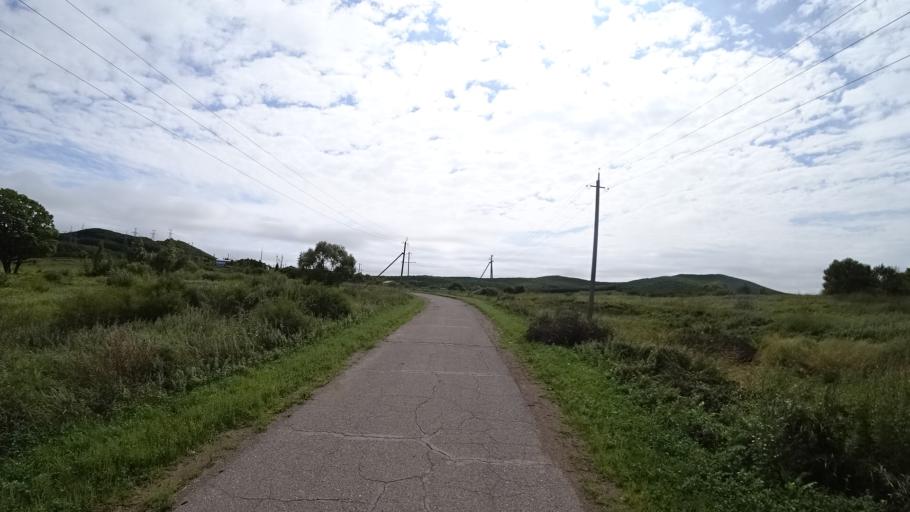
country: RU
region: Primorskiy
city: Lyalichi
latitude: 44.1328
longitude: 132.3877
